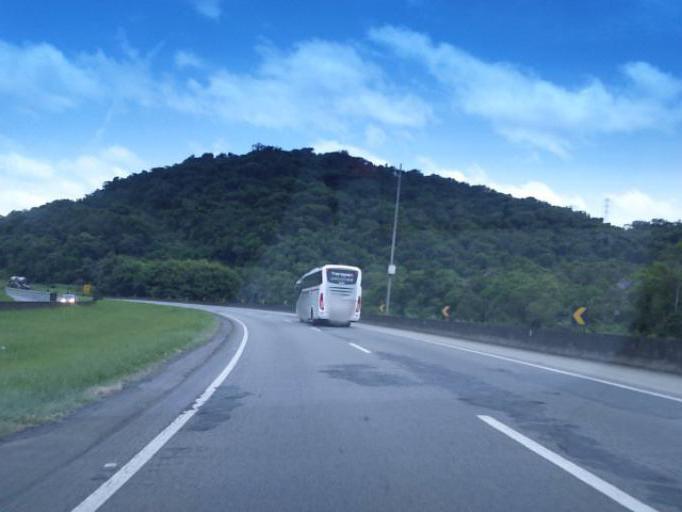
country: BR
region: Sao Paulo
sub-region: Juquia
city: Juquia
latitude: -24.3808
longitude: -47.7144
